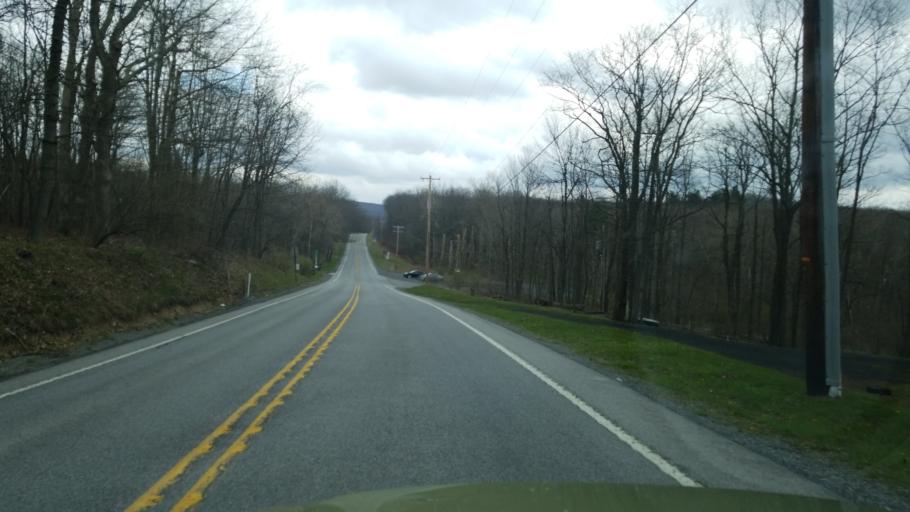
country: US
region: Pennsylvania
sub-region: Blair County
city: Tipton
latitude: 40.7249
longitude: -78.3547
